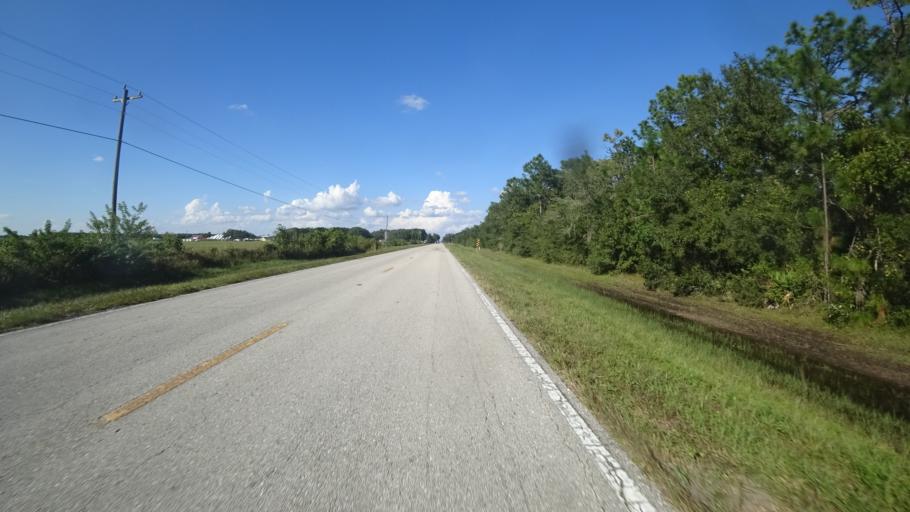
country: US
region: Florida
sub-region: Sarasota County
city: The Meadows
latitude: 27.4406
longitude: -82.3035
